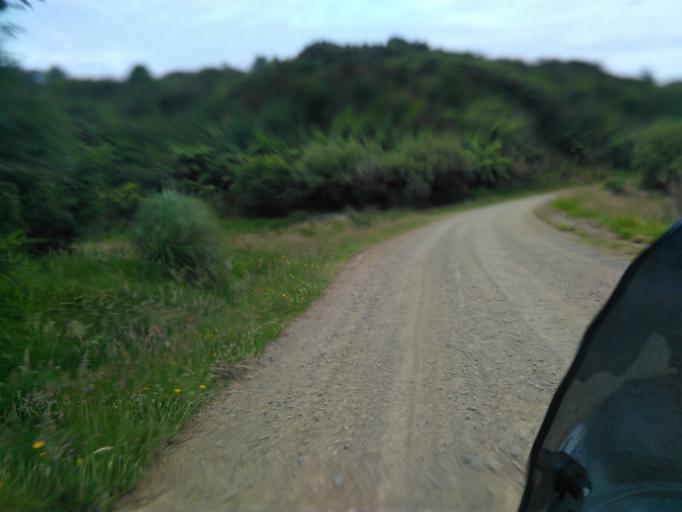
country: NZ
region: Bay of Plenty
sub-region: Opotiki District
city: Opotiki
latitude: -38.0168
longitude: 177.4280
